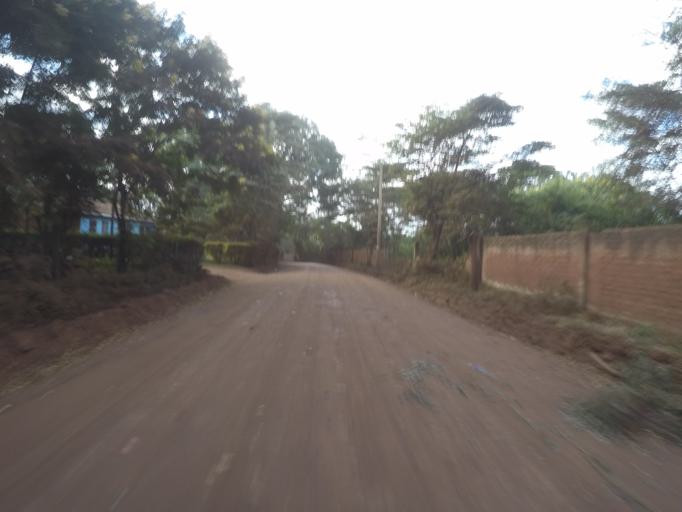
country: TZ
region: Arusha
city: Kiratu
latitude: -3.3371
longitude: 35.6669
